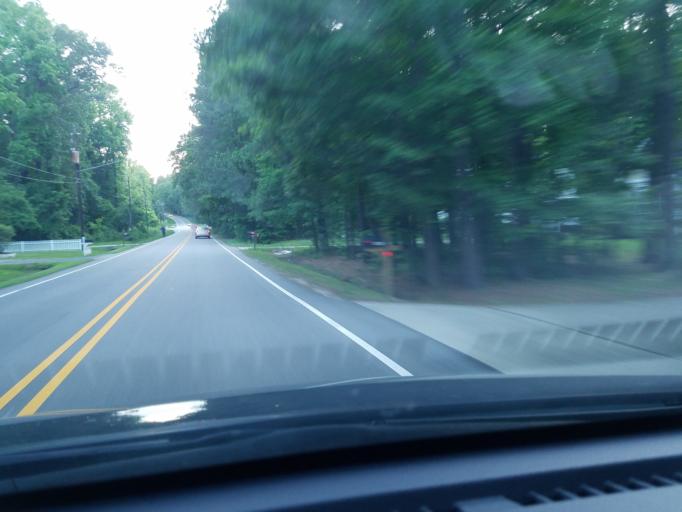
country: US
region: North Carolina
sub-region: Durham County
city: Durham
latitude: 35.9359
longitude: -78.9469
